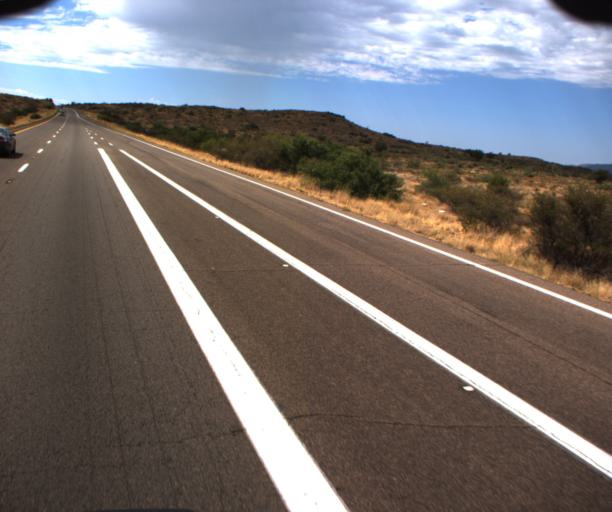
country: US
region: Arizona
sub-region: Yavapai County
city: Cordes Lakes
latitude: 34.2307
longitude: -112.1167
